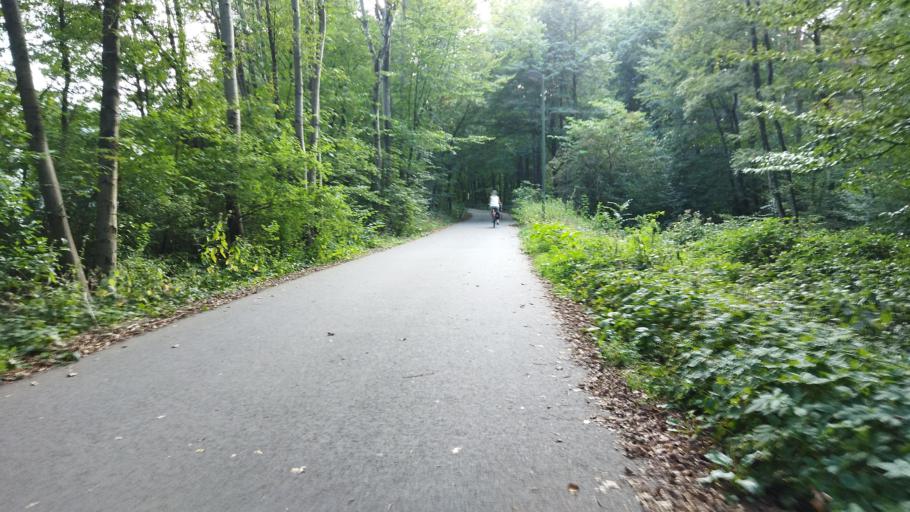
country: DE
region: Lower Saxony
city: Osnabrueck
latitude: 52.2478
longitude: 8.0299
